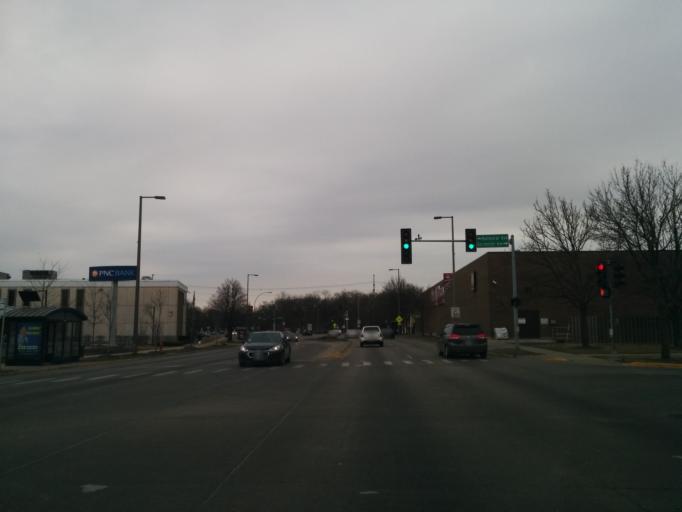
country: US
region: Illinois
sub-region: Cook County
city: Westchester
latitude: 41.8505
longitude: -87.8818
